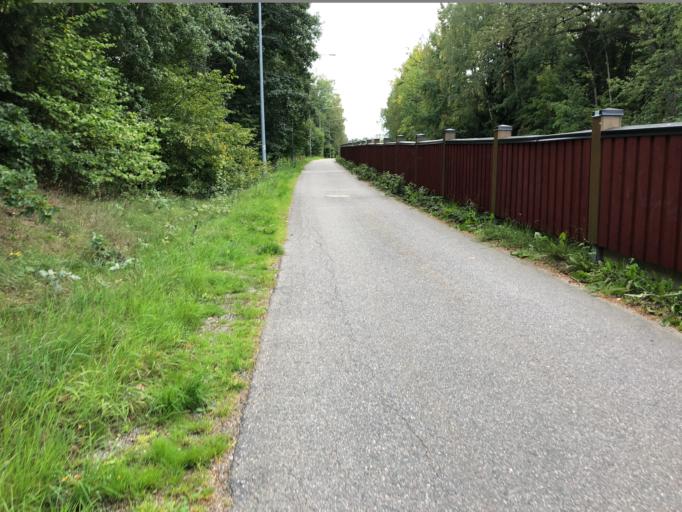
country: SE
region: Stockholm
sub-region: Tyreso Kommun
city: Bollmora
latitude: 59.2073
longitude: 18.2065
